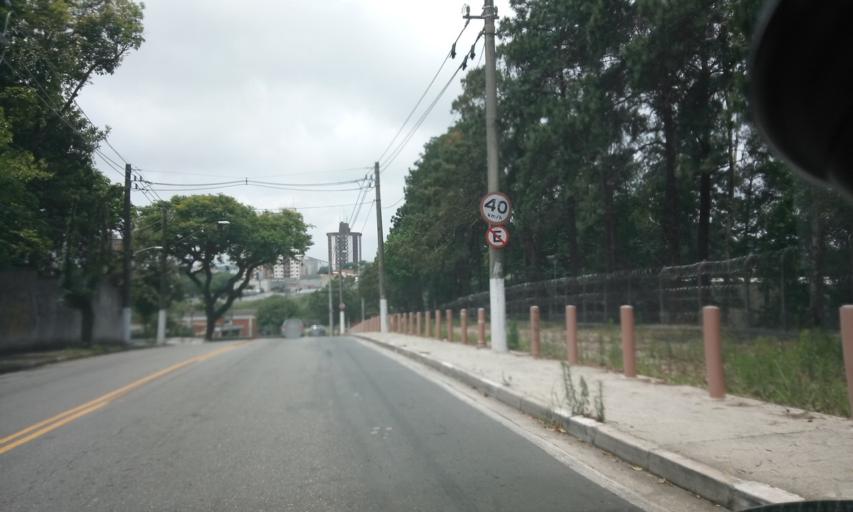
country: BR
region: Sao Paulo
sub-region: Sao Bernardo Do Campo
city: Sao Bernardo do Campo
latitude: -23.6992
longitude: -46.5653
